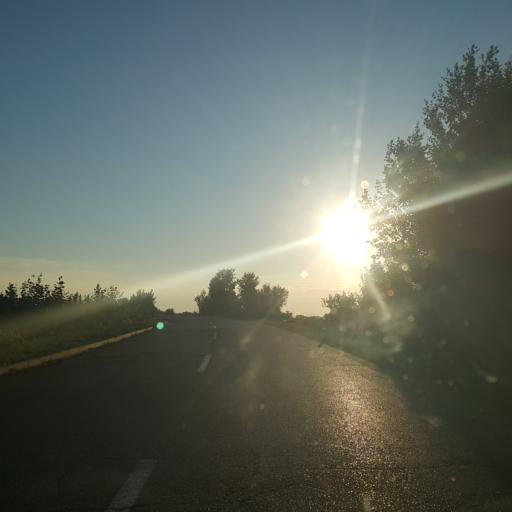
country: RS
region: Central Serbia
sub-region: Borski Okrug
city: Negotin
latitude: 44.2095
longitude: 22.4569
